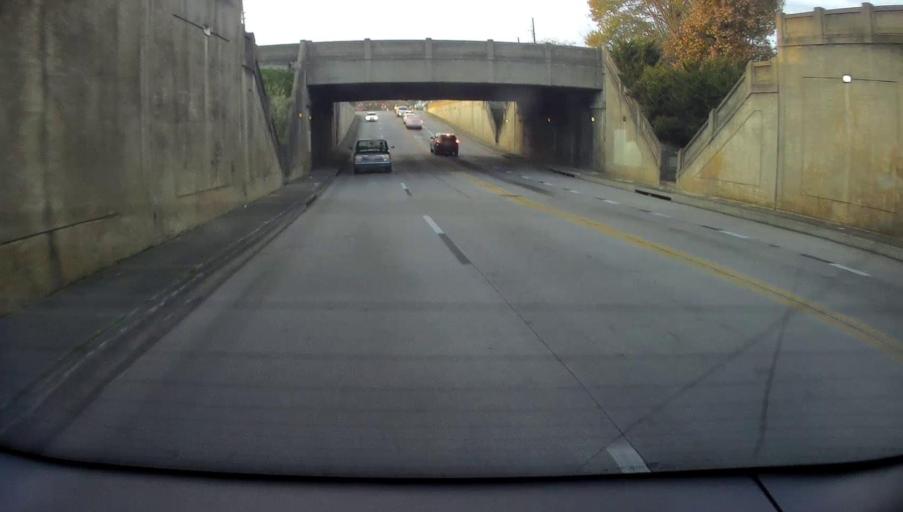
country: US
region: Alabama
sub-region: Etowah County
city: Attalla
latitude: 34.0209
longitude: -86.0873
